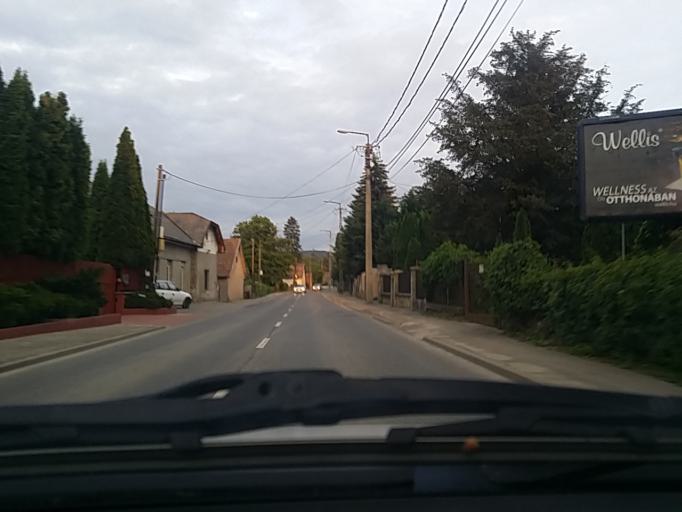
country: HU
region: Pest
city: Solymar
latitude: 47.5685
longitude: 18.9511
